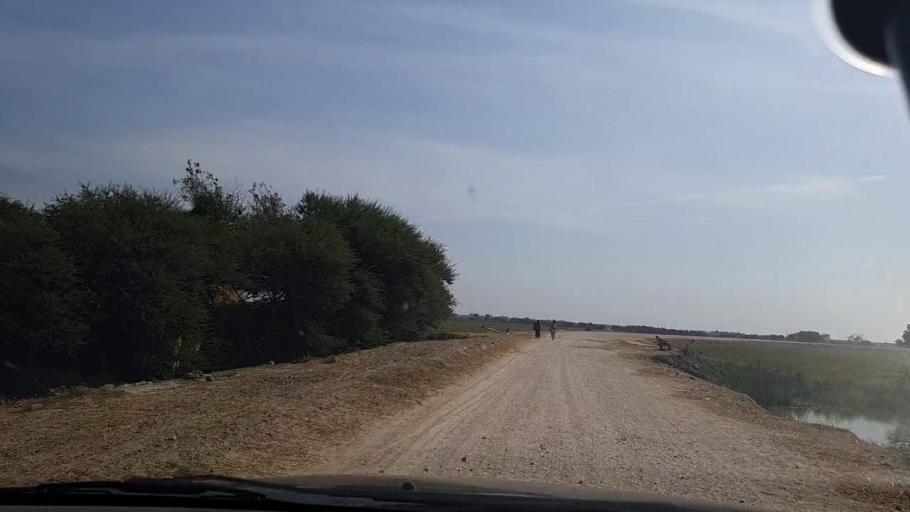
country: PK
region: Sindh
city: Mirpur Batoro
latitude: 24.7321
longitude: 68.2757
